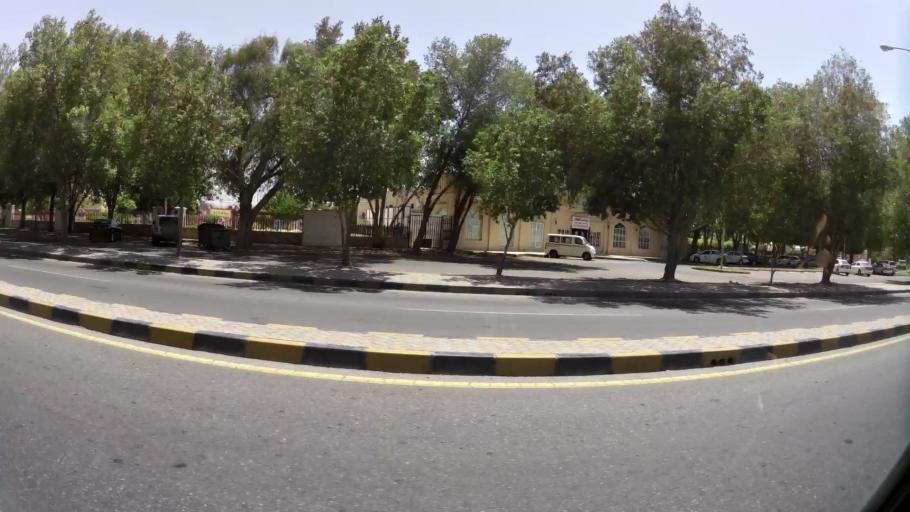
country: OM
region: Muhafazat Masqat
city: Muscat
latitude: 23.6212
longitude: 58.4939
